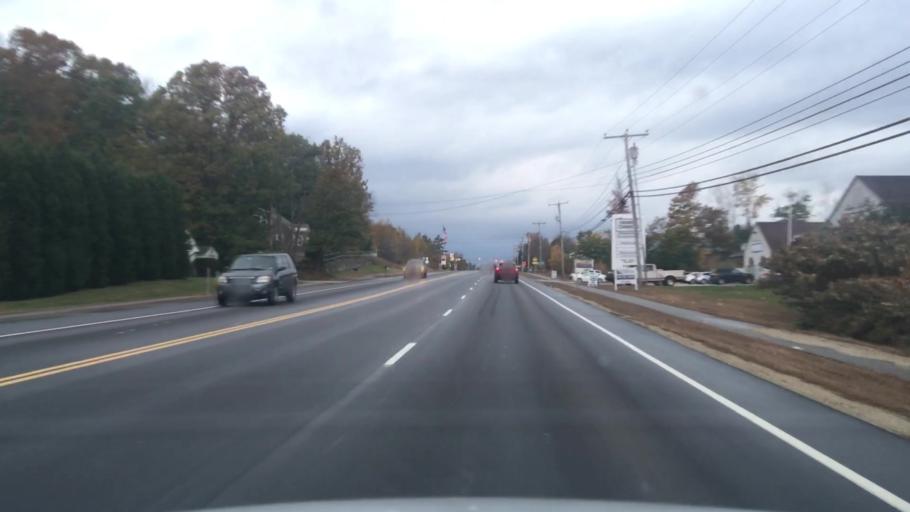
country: US
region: New Hampshire
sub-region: Merrimack County
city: Chichester
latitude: 43.2418
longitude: -71.3995
